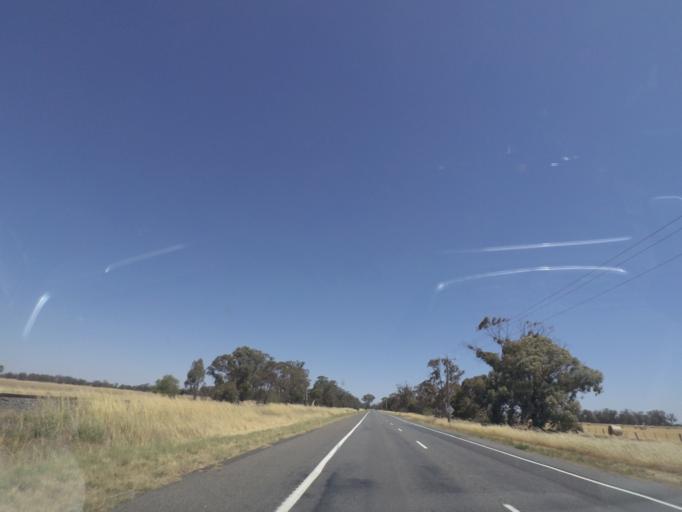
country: AU
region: Victoria
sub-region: Greater Shepparton
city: Shepparton
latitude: -36.2218
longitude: 145.4318
